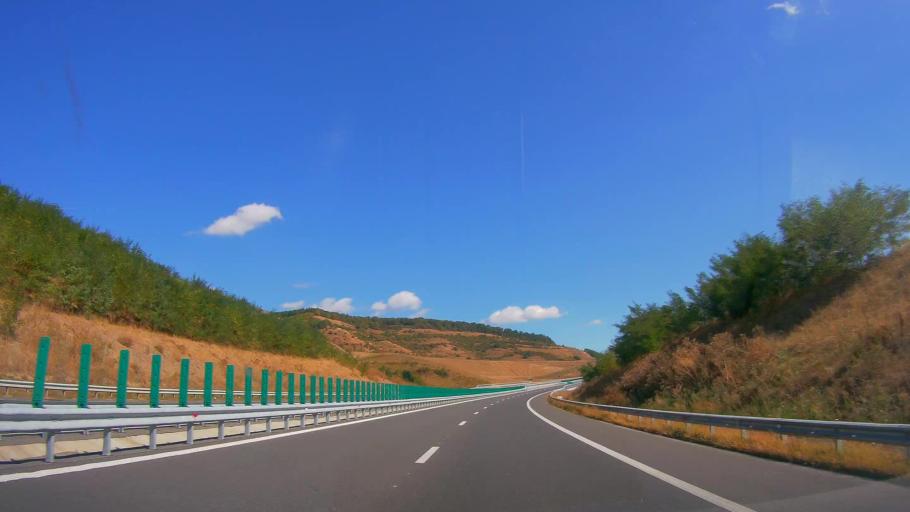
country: RO
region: Cluj
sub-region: Comuna Gilau
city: Gilau
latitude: 46.7758
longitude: 23.3895
